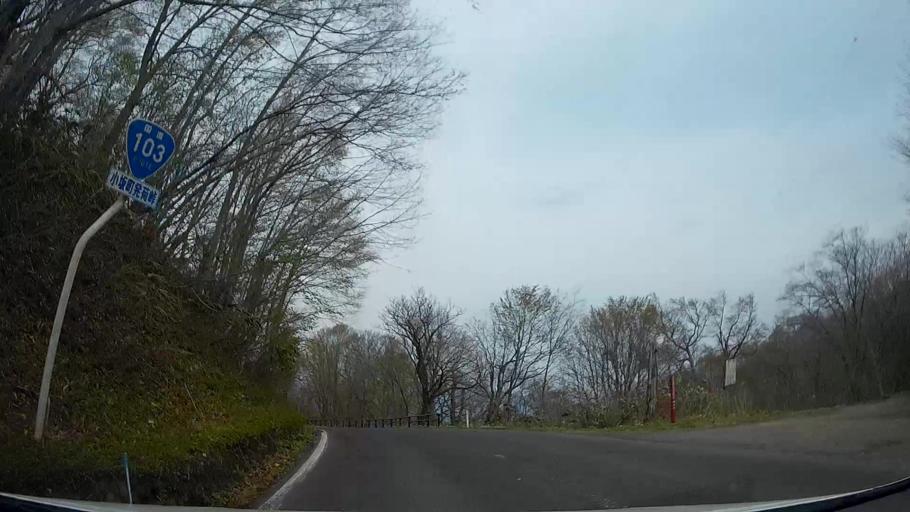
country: JP
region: Akita
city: Hanawa
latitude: 40.4065
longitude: 140.8653
